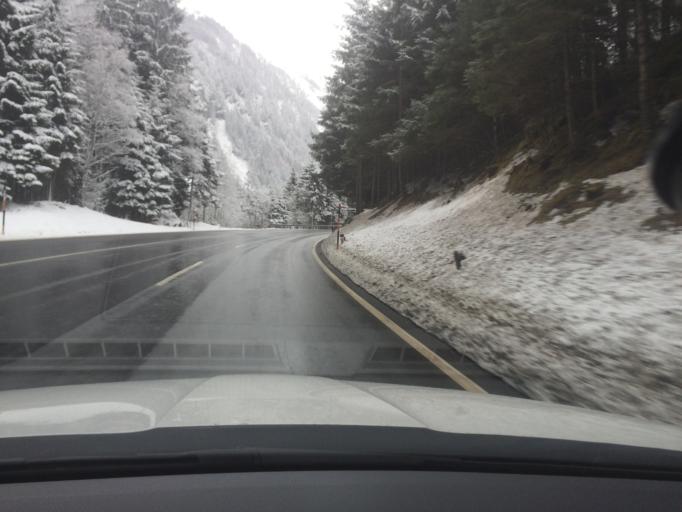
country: AT
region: Salzburg
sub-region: Politischer Bezirk Zell am See
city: Mittersill
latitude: 47.2209
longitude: 12.4972
